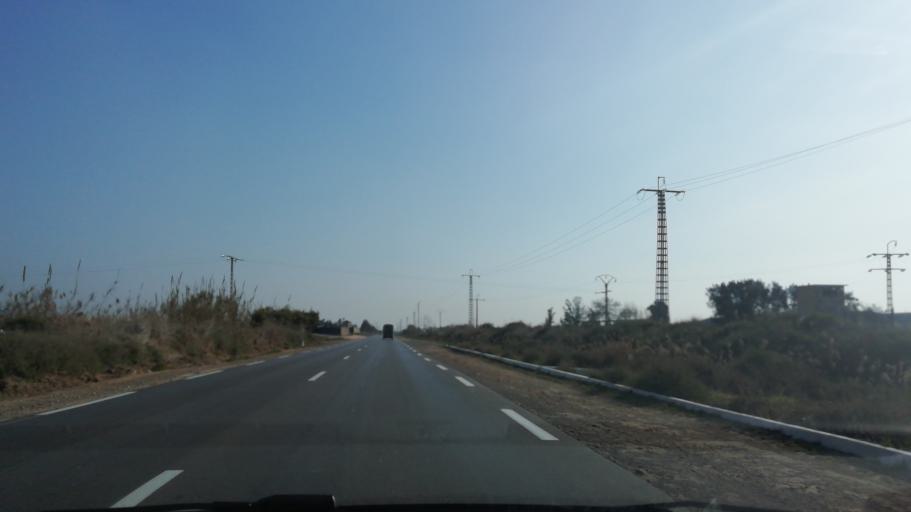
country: DZ
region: Mostaganem
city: Mostaganem
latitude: 35.7443
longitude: 0.0146
